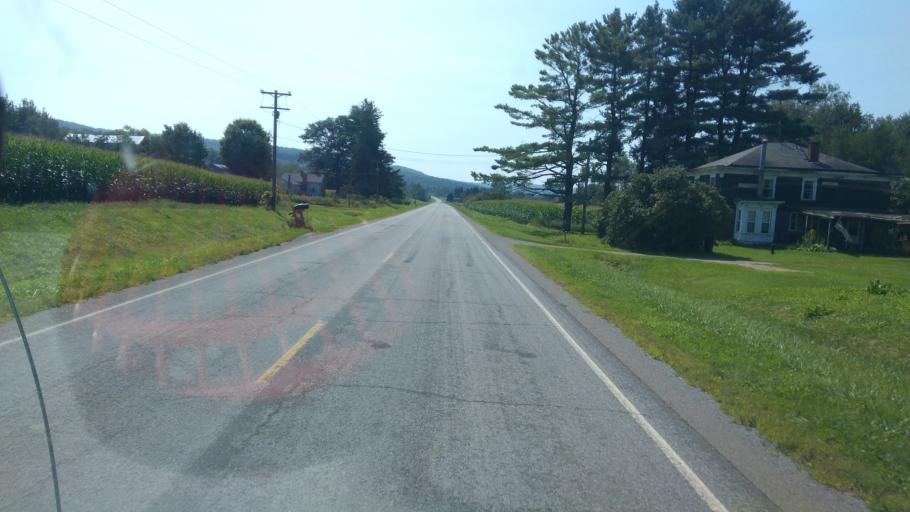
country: US
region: New York
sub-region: Allegany County
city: Belmont
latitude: 42.3440
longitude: -77.9281
